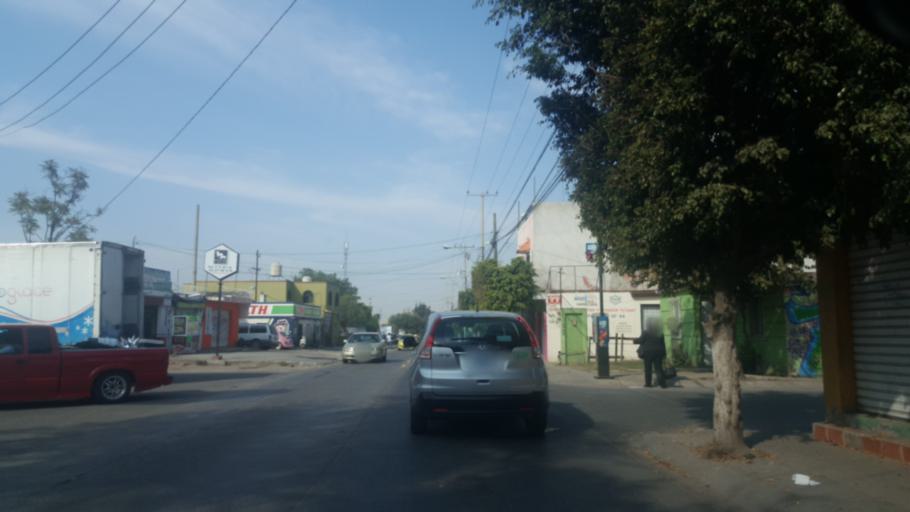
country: MX
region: Guanajuato
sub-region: Leon
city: Fraccionamiento Paraiso Real
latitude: 21.1029
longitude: -101.6152
